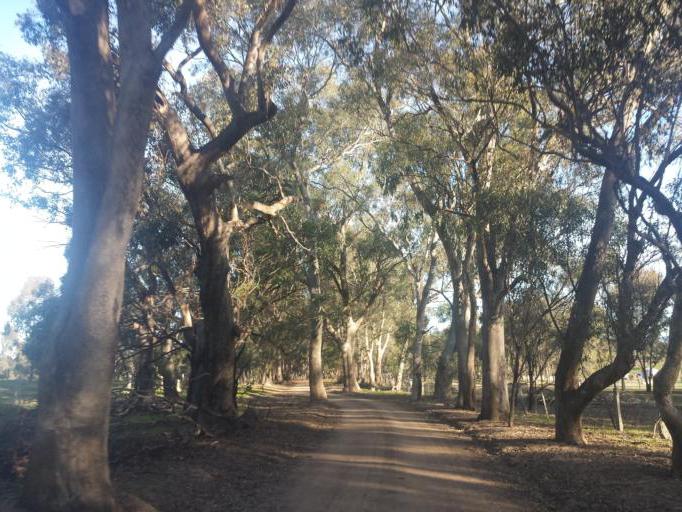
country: AU
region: Victoria
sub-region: Murrindindi
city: Kinglake West
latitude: -37.0142
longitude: 145.2318
